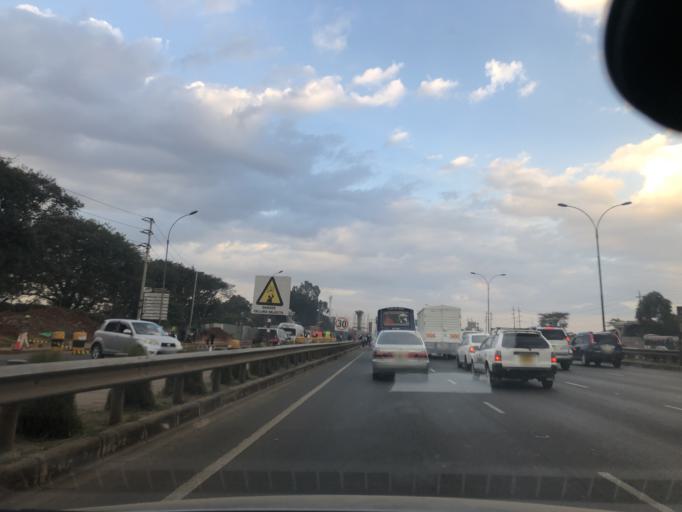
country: KE
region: Nairobi Area
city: Pumwani
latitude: -1.2492
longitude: 36.8626
